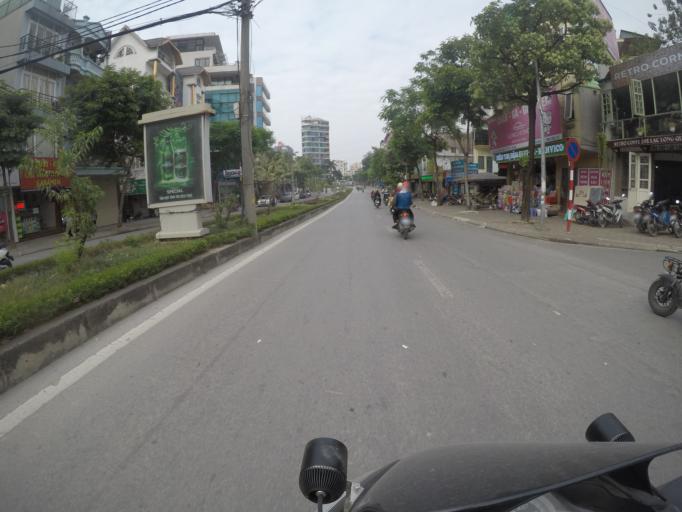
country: VN
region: Ha Noi
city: Tay Ho
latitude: 21.0599
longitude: 105.8090
